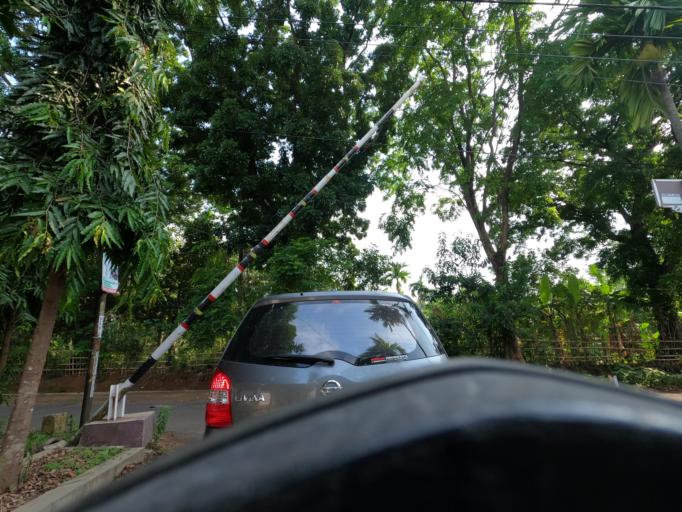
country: ID
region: West Java
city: Lembang
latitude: -6.5775
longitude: 107.7711
